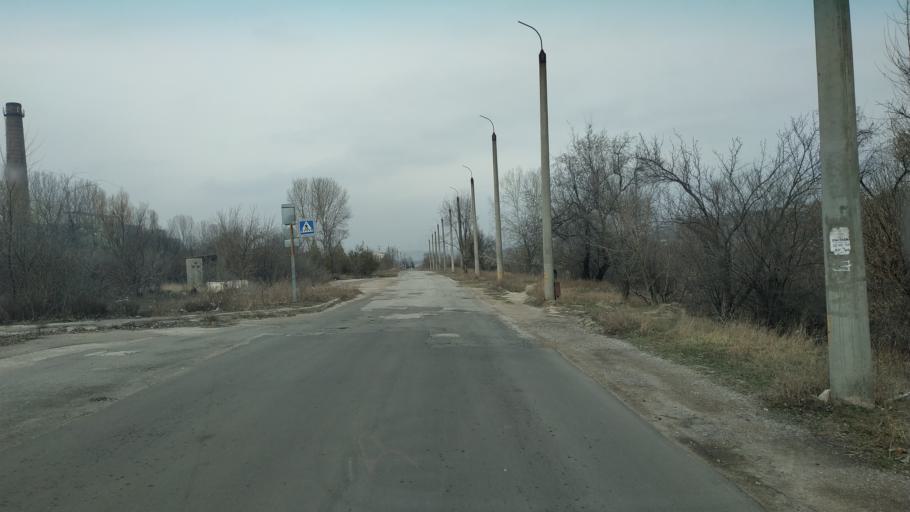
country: MD
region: Chisinau
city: Singera
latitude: 46.9038
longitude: 29.0192
